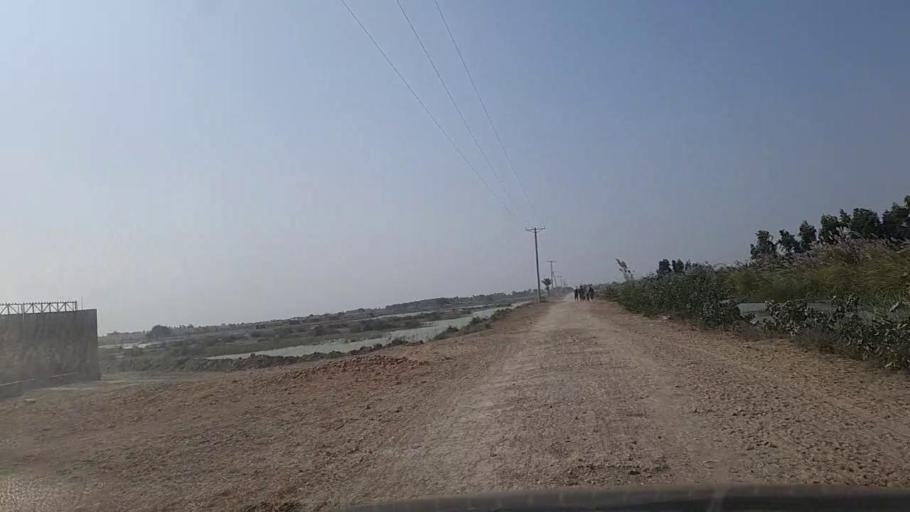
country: PK
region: Sindh
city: Gharo
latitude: 24.6845
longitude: 67.6018
